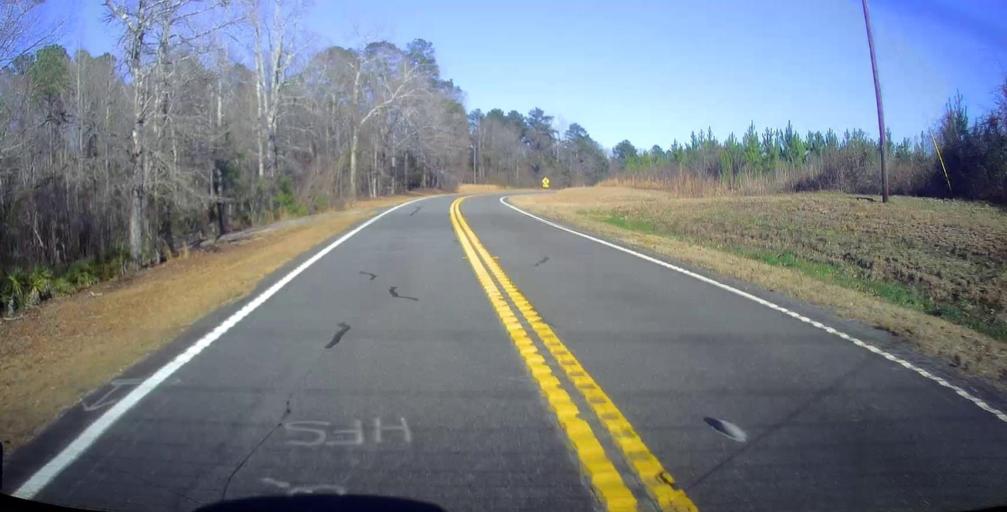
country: US
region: Georgia
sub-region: Talbot County
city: Talbotton
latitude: 32.6464
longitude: -84.4255
